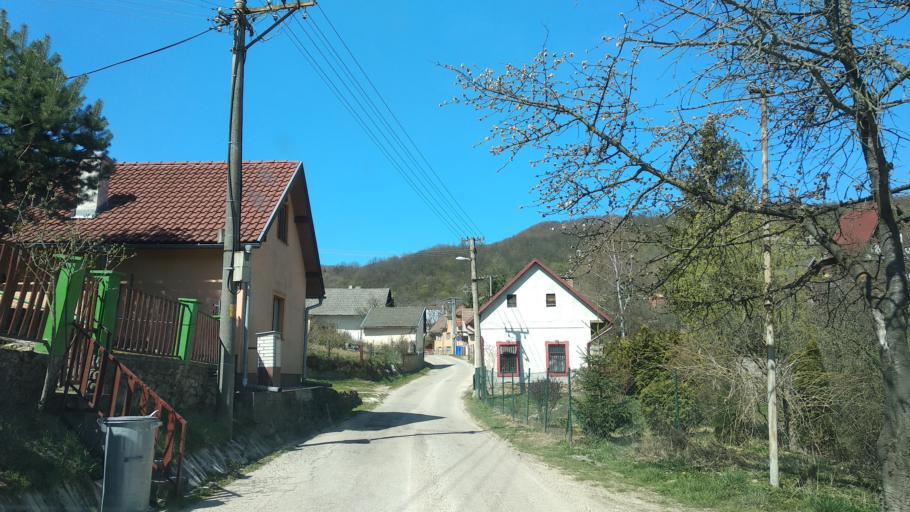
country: SK
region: Nitriansky
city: Trencianske Teplice
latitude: 48.8707
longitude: 18.1736
